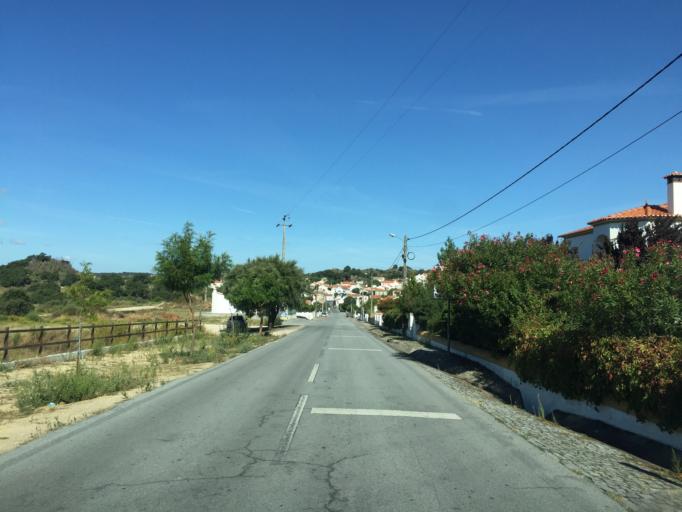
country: PT
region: Portalegre
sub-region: Marvao
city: Marvao
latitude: 39.4435
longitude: -7.3683
